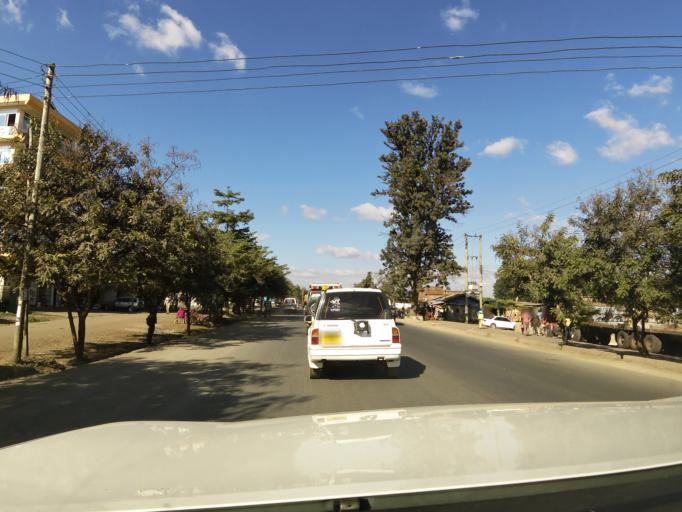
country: TZ
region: Arusha
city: Arusha
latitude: -3.3759
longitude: 36.6675
